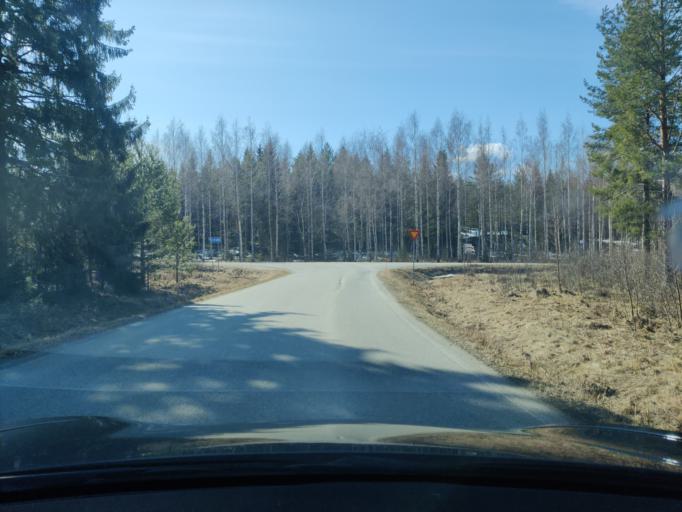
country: FI
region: Northern Savo
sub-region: Kuopio
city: Vehmersalmi
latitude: 62.7720
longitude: 27.9782
